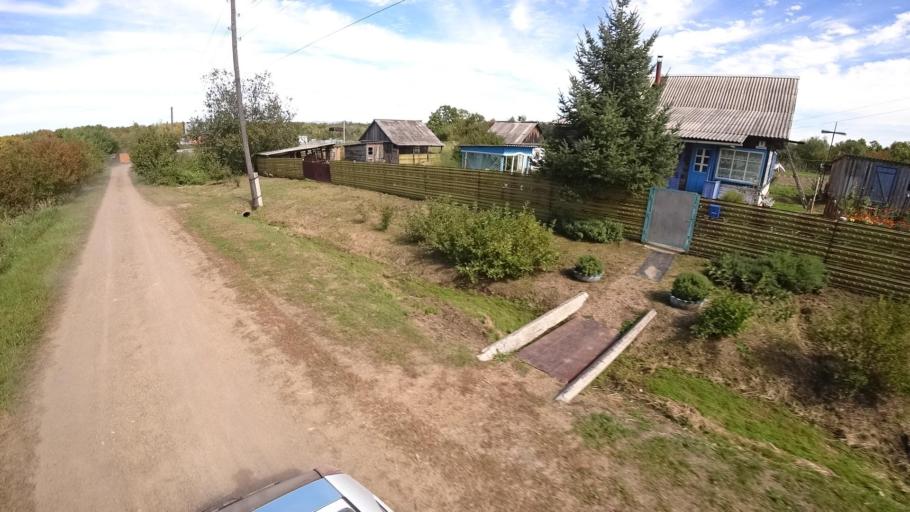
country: RU
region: Primorskiy
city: Yakovlevka
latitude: 44.4364
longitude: 133.5609
